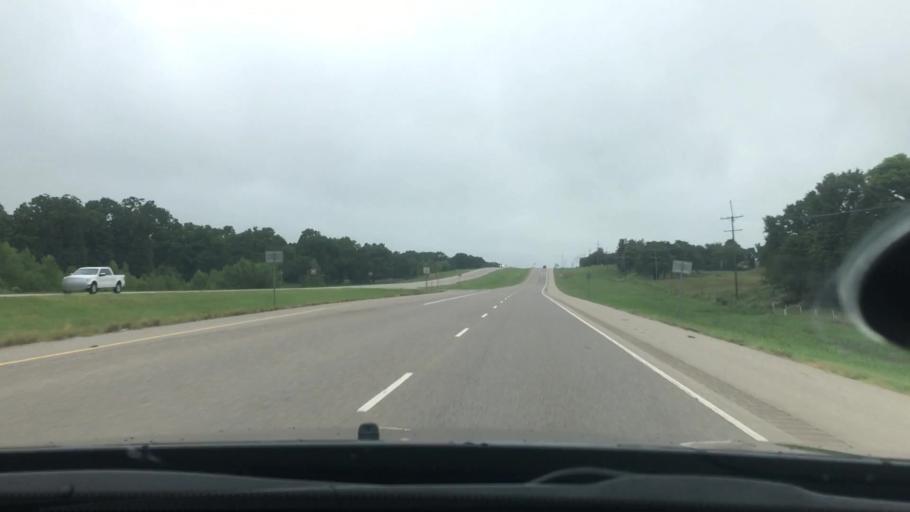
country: US
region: Oklahoma
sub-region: Seminole County
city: Seminole
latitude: 35.3395
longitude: -96.6715
